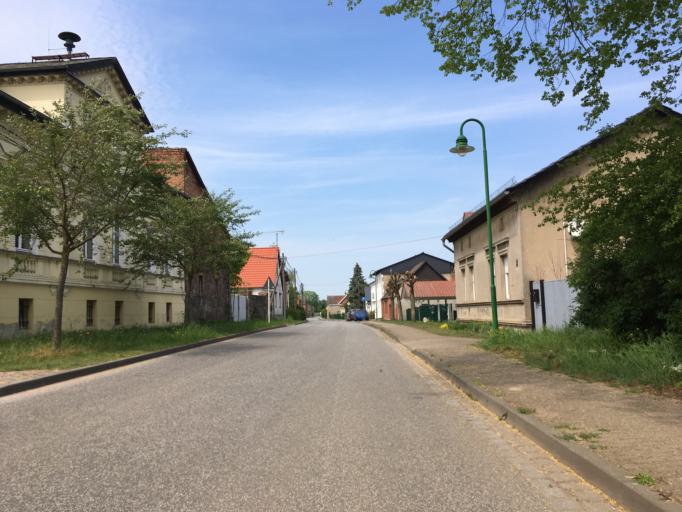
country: DE
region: Brandenburg
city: Biesenthal
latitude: 52.7344
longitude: 13.6659
